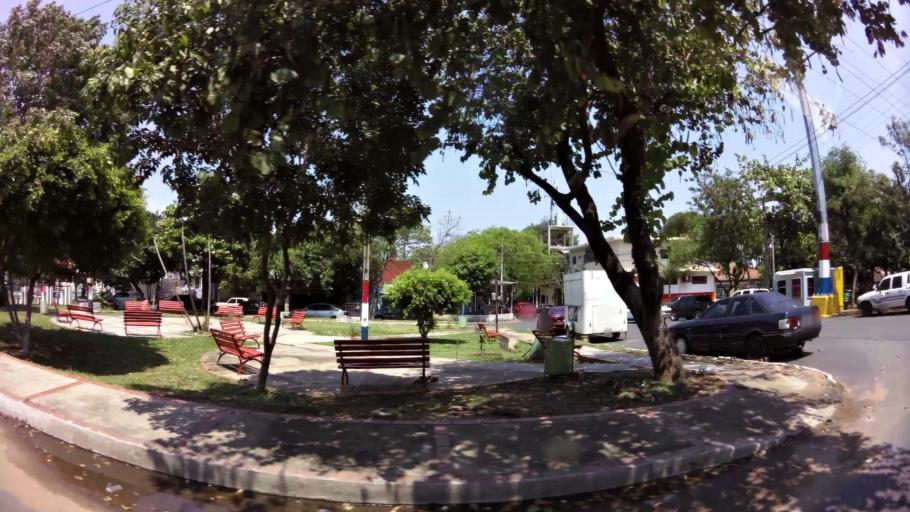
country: PY
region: Asuncion
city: Asuncion
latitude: -25.3028
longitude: -57.6516
